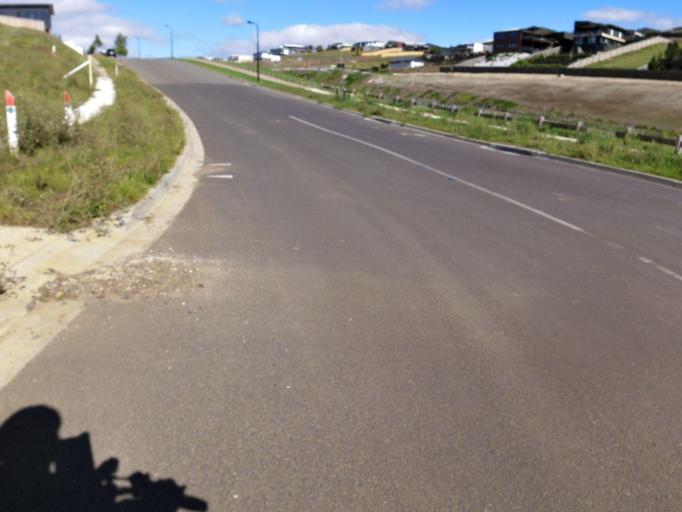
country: AU
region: Victoria
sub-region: Greater Geelong
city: Wandana Heights
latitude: -38.1557
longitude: 144.3013
